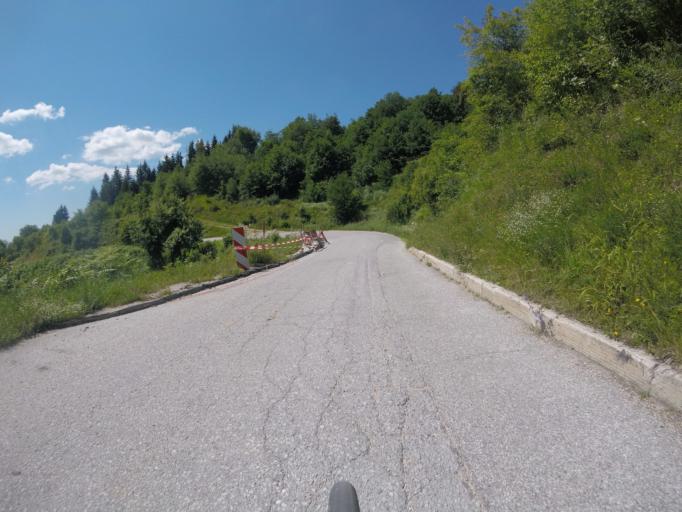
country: SI
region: Kostanjevica na Krki
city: Kostanjevica na Krki
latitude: 45.7759
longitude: 15.4685
